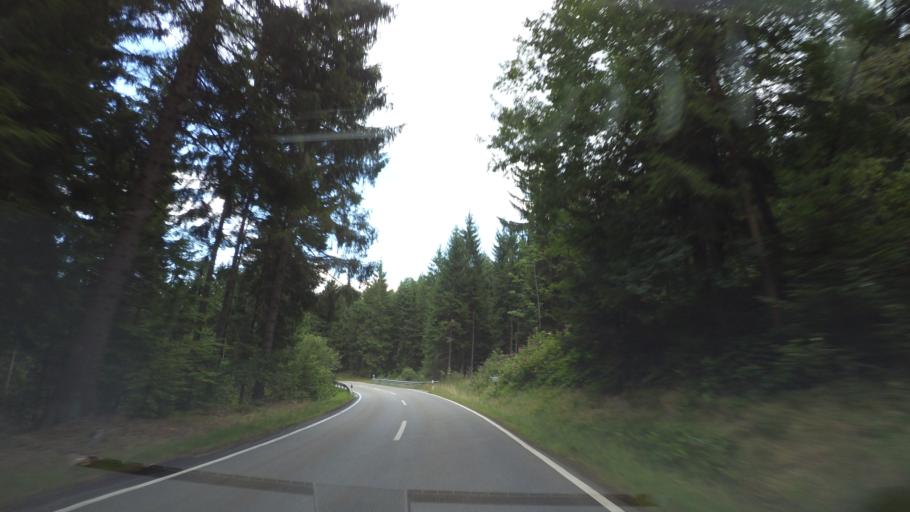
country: DE
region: Bavaria
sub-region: Upper Palatinate
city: Arrach
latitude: 49.1746
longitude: 13.0039
